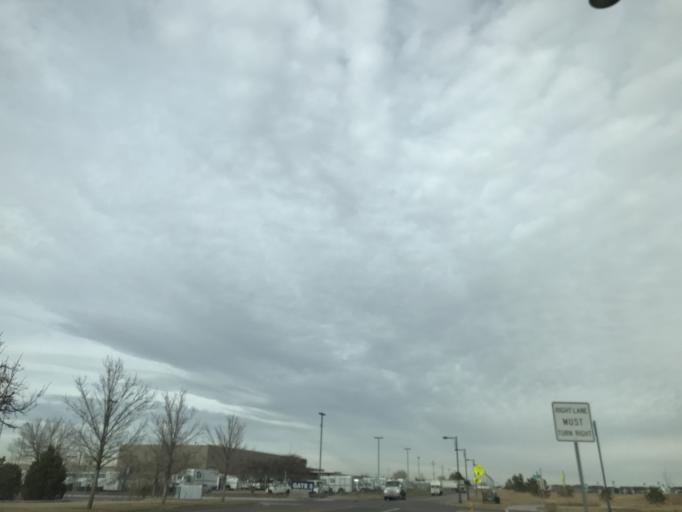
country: US
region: Colorado
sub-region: Adams County
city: Commerce City
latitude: 39.7864
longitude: -104.8979
